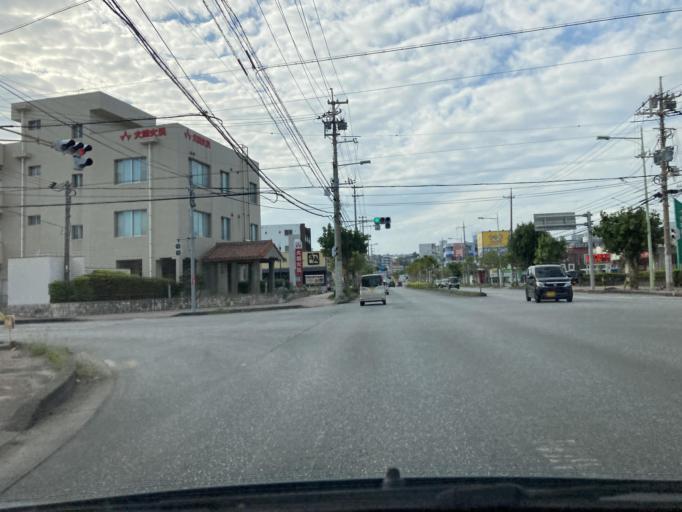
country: JP
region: Okinawa
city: Okinawa
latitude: 26.3174
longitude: 127.8250
